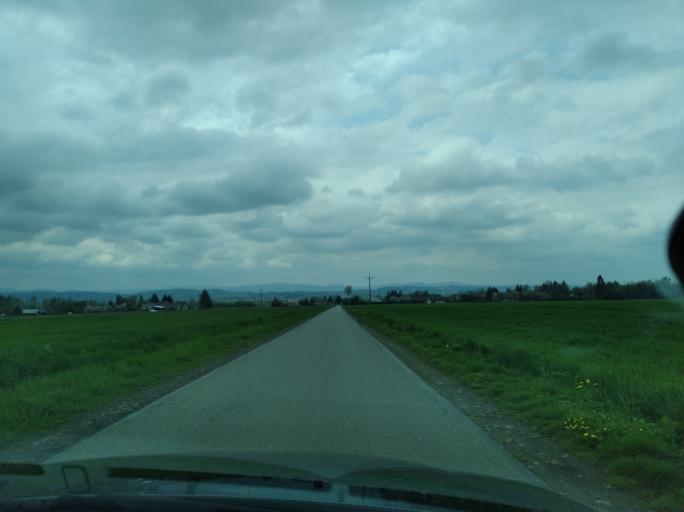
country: PL
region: Subcarpathian Voivodeship
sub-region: Powiat brzozowski
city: Gorki
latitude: 49.6225
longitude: 22.0132
